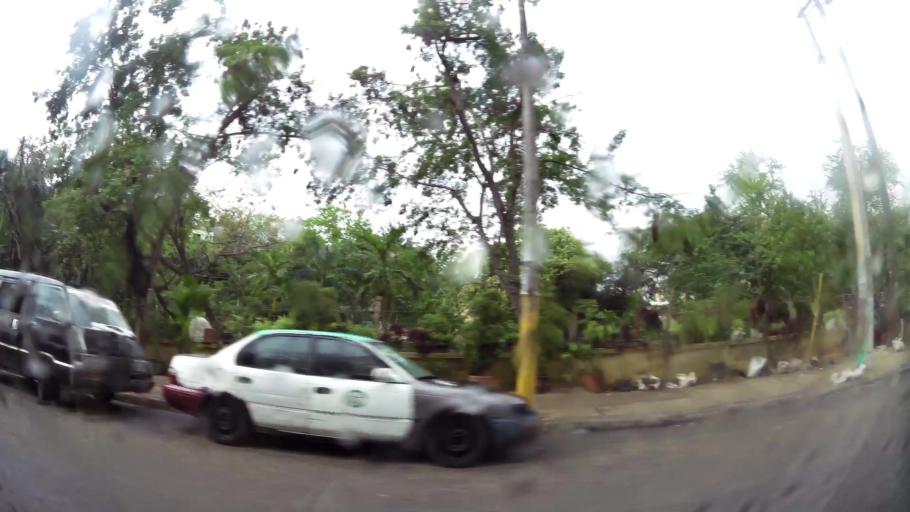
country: DO
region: Nacional
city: La Agustina
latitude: 18.4977
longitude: -69.9313
